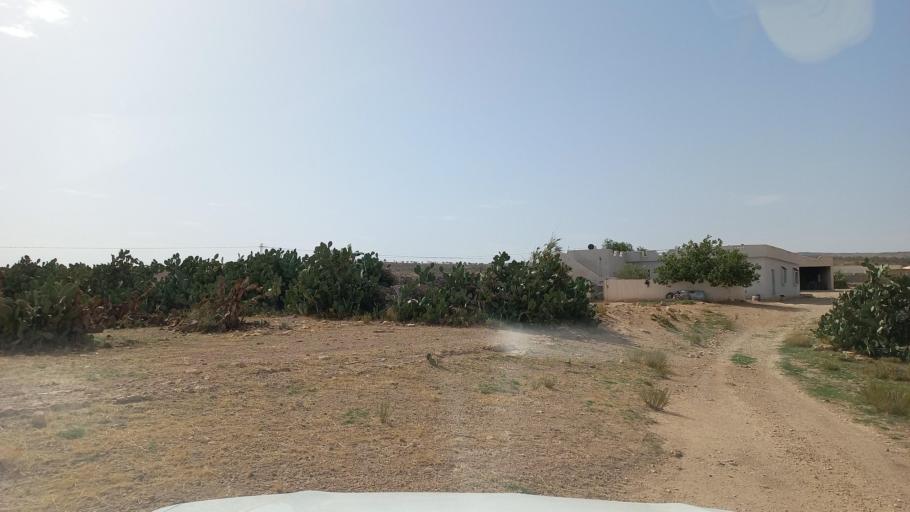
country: TN
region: Al Qasrayn
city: Kasserine
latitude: 35.3018
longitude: 8.9385
